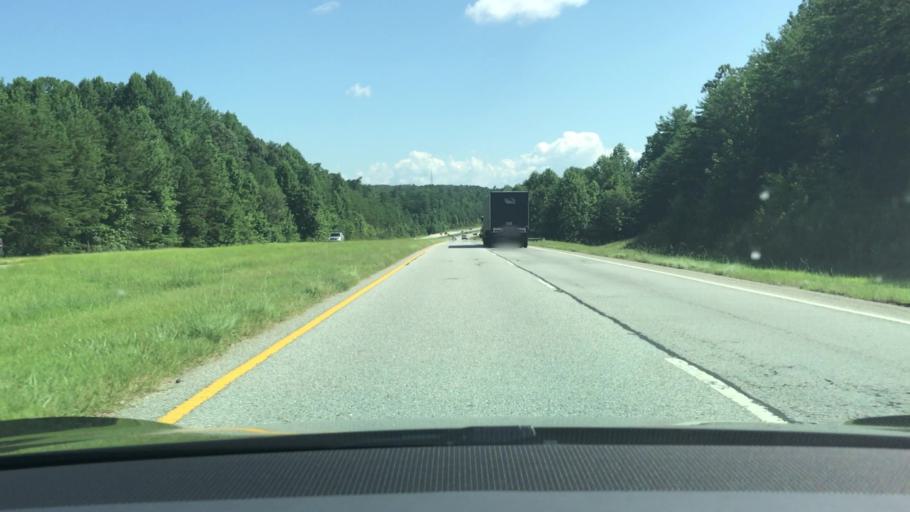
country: US
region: Georgia
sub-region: Habersham County
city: Clarkesville
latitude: 34.6924
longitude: -83.4226
